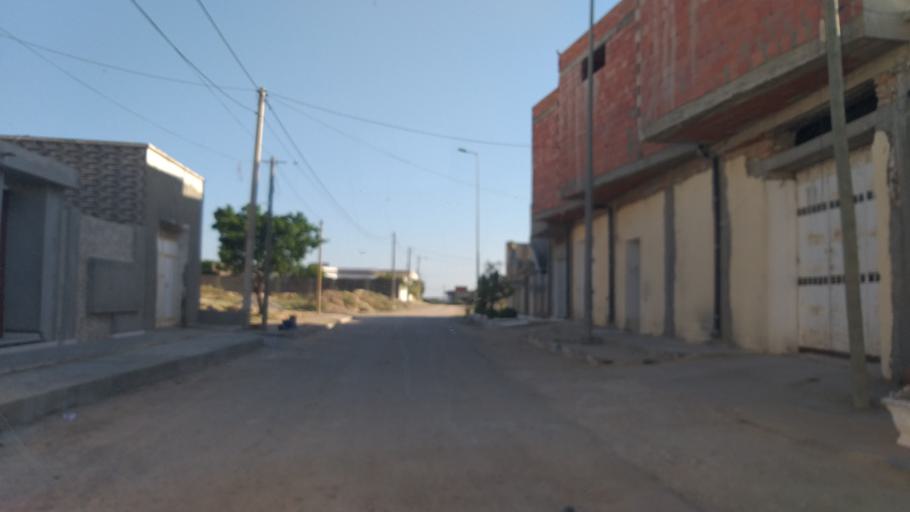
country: TN
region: Al Mahdiyah
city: El Jem
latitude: 35.2835
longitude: 10.7111
